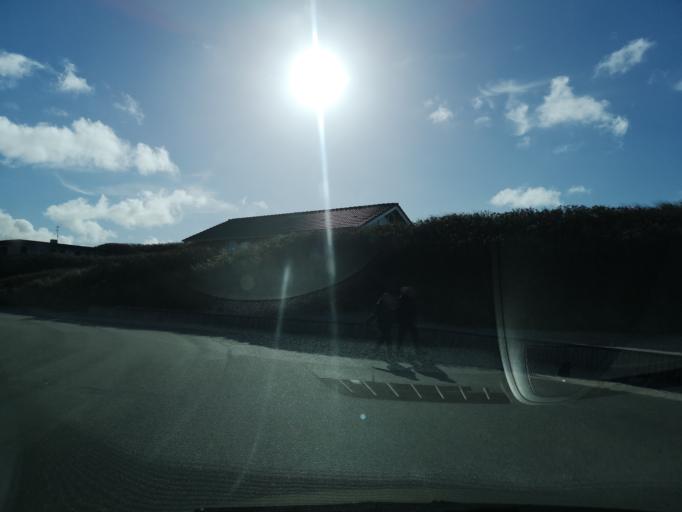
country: DK
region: South Denmark
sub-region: Varde Kommune
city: Oksbol
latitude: 55.7433
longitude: 8.1751
